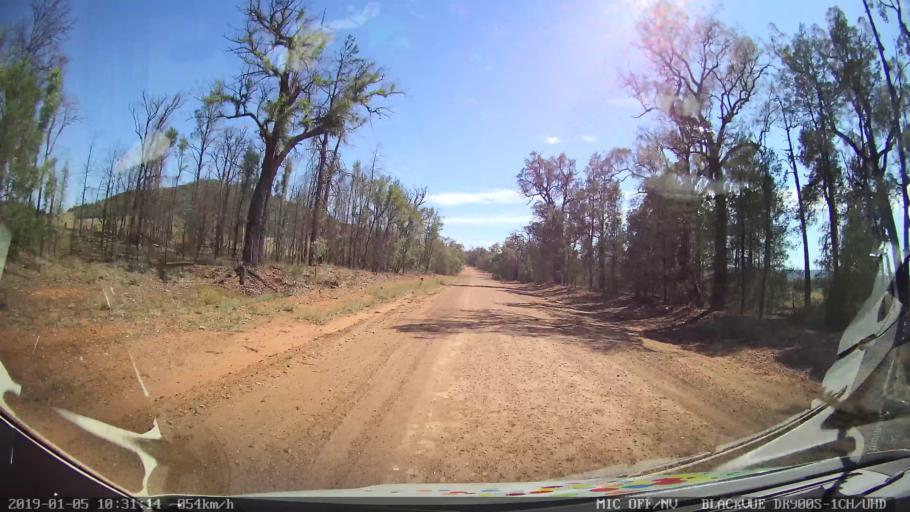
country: AU
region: New South Wales
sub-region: Gilgandra
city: Gilgandra
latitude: -31.5260
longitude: 148.9272
